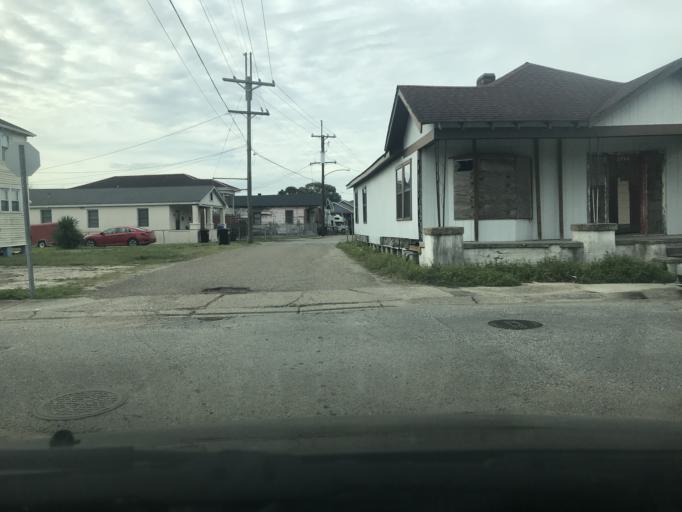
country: US
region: Louisiana
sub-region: Orleans Parish
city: New Orleans
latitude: 29.9555
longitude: -90.1098
